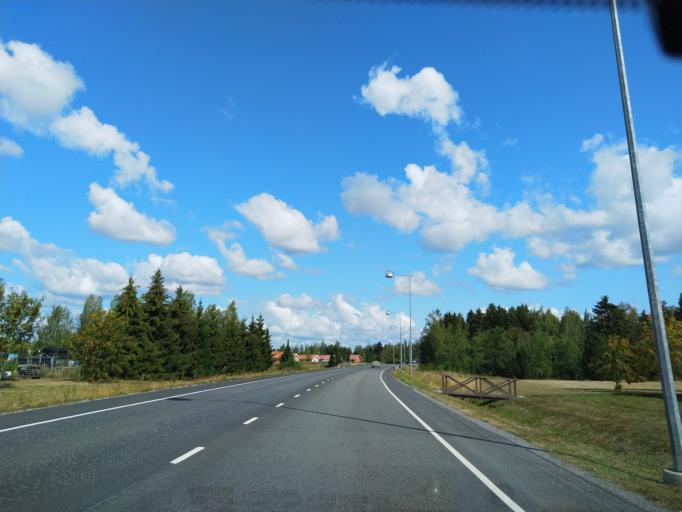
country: FI
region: Satakunta
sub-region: Pori
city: Huittinen
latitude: 61.1703
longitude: 22.7082
